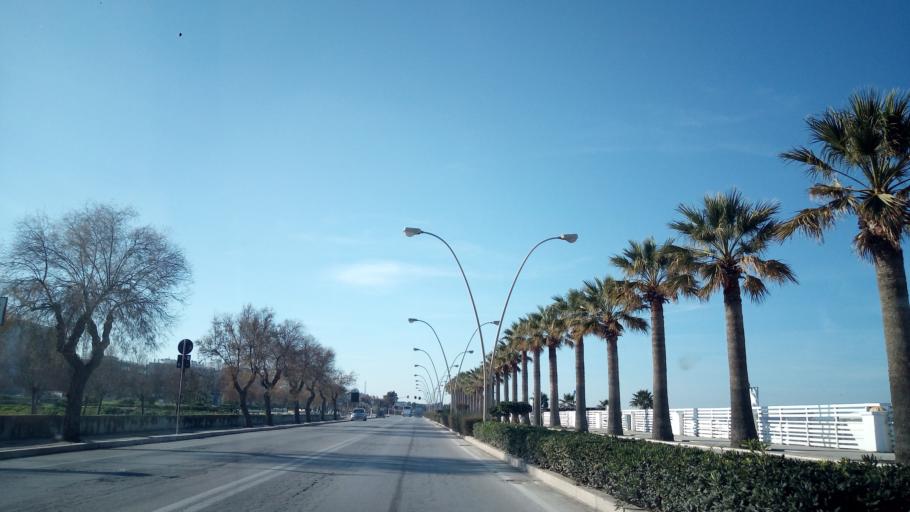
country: IT
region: Apulia
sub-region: Provincia di Barletta - Andria - Trani
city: Barletta
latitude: 41.3233
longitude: 16.2778
